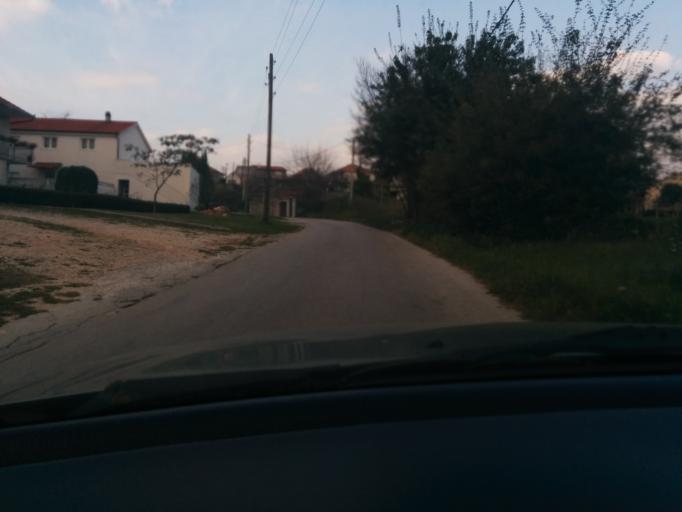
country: HR
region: Splitsko-Dalmatinska
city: Sinj
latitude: 43.7063
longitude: 16.6528
